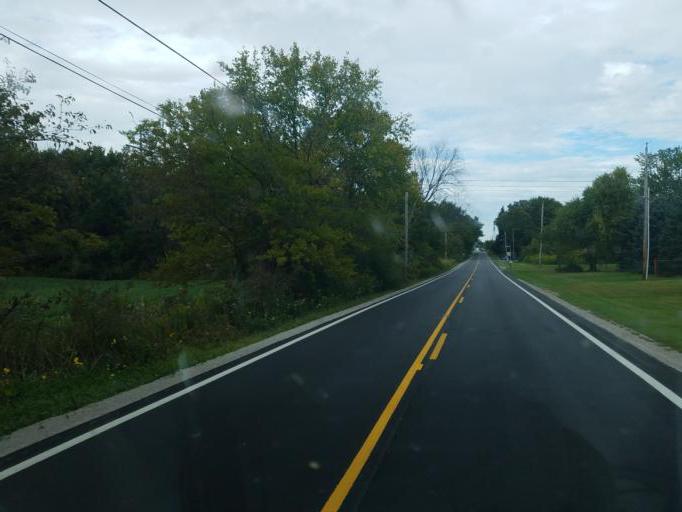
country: US
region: Ohio
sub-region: Franklin County
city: New Albany
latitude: 40.1179
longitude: -82.8108
